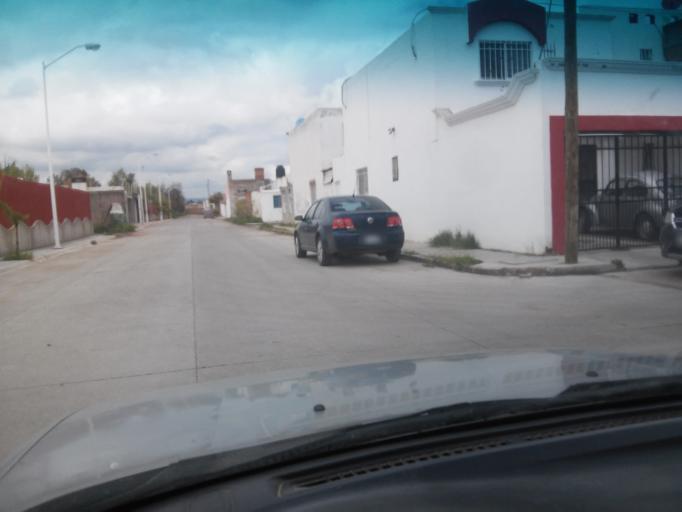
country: MX
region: Durango
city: Victoria de Durango
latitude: 24.0060
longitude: -104.6359
